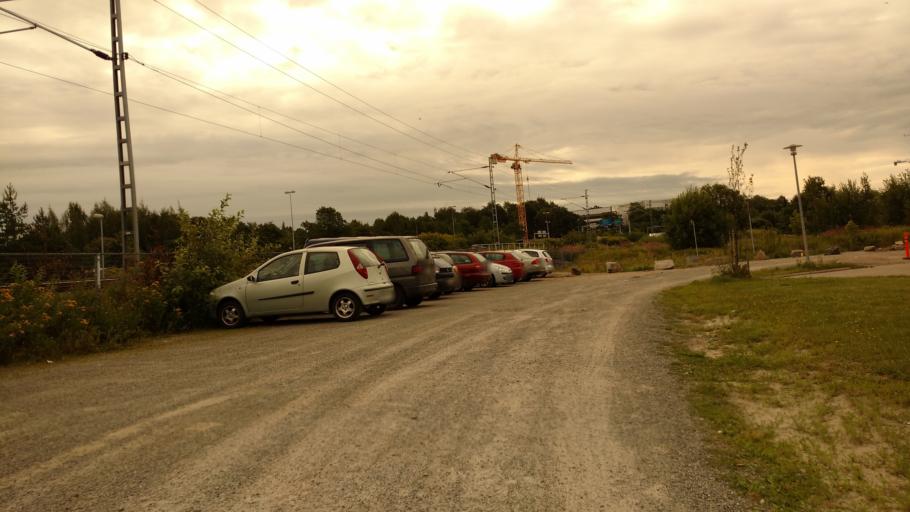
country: FI
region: Varsinais-Suomi
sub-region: Turku
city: Turku
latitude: 60.4591
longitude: 22.2869
